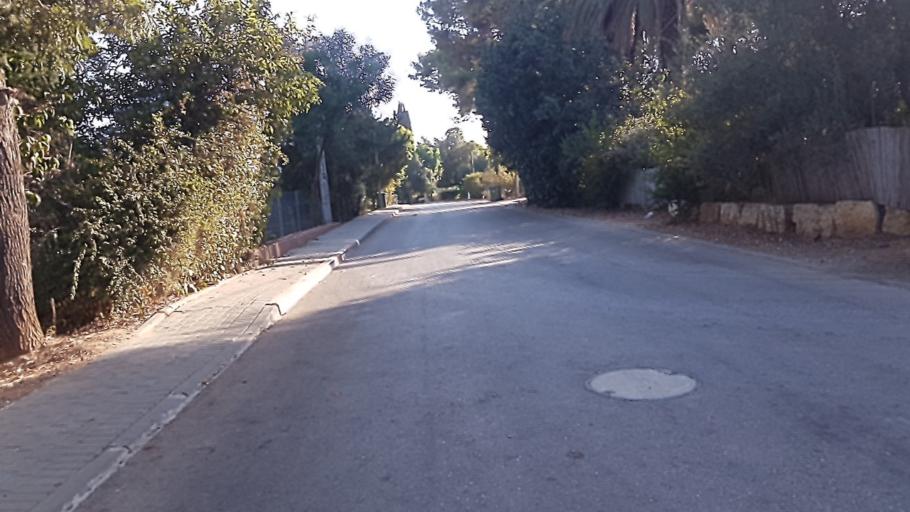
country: IL
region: Central District
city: Hod HaSharon
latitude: 32.1431
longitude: 34.9038
